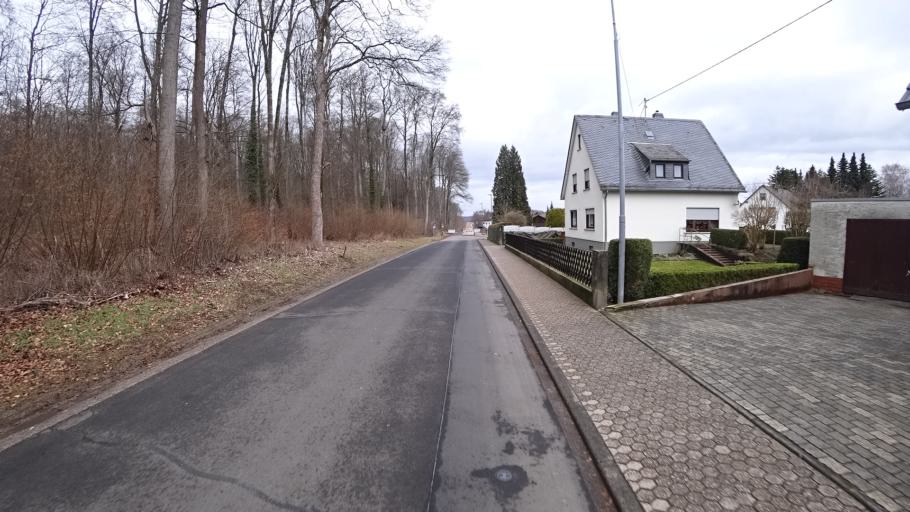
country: DE
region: Rheinland-Pfalz
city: Dernbach
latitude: 50.4303
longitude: 7.7916
